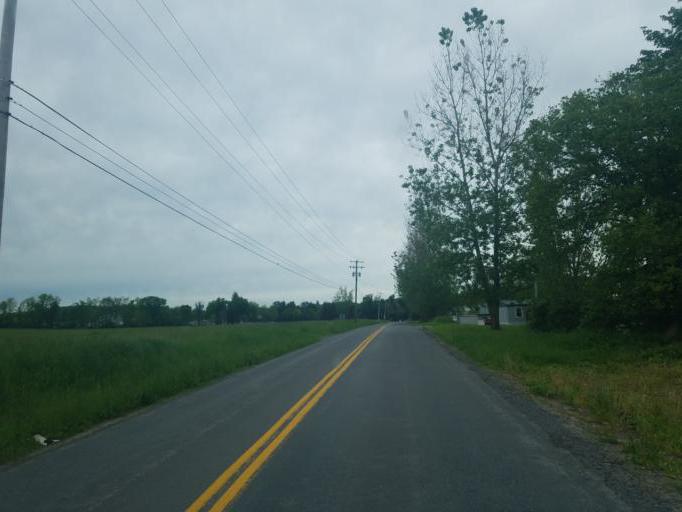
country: US
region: New York
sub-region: Herkimer County
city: Frankfort
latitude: 42.9278
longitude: -75.1214
